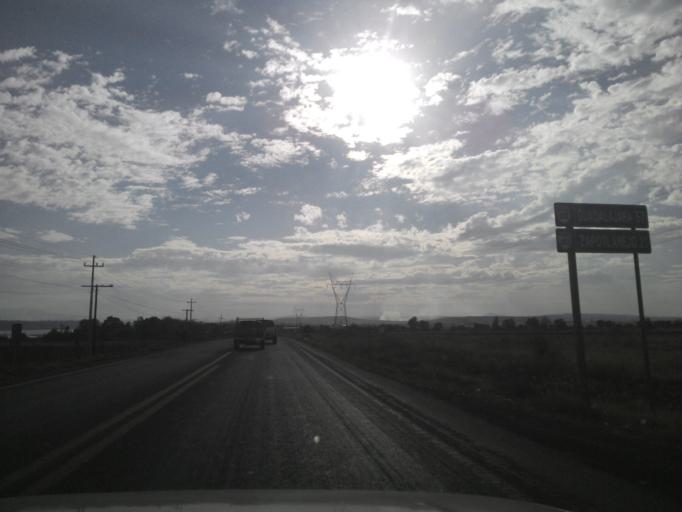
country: MX
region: Jalisco
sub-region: Acatic
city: Tierras Coloradas
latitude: 20.7207
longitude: -102.9082
